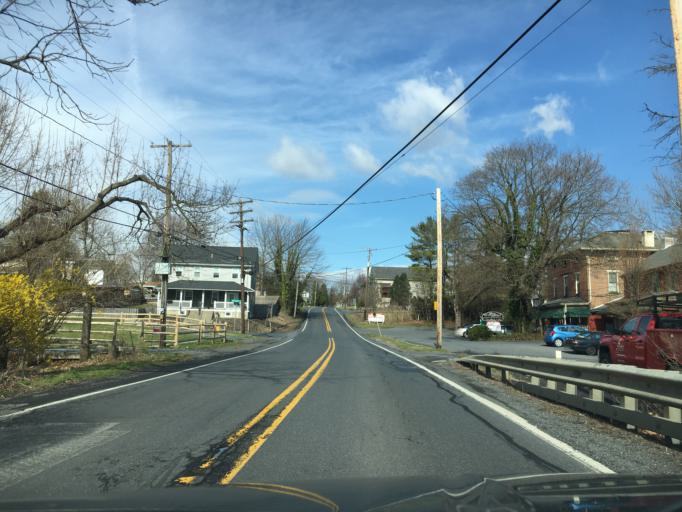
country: US
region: Pennsylvania
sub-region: Northampton County
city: North Catasauqua
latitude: 40.6883
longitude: -75.4516
